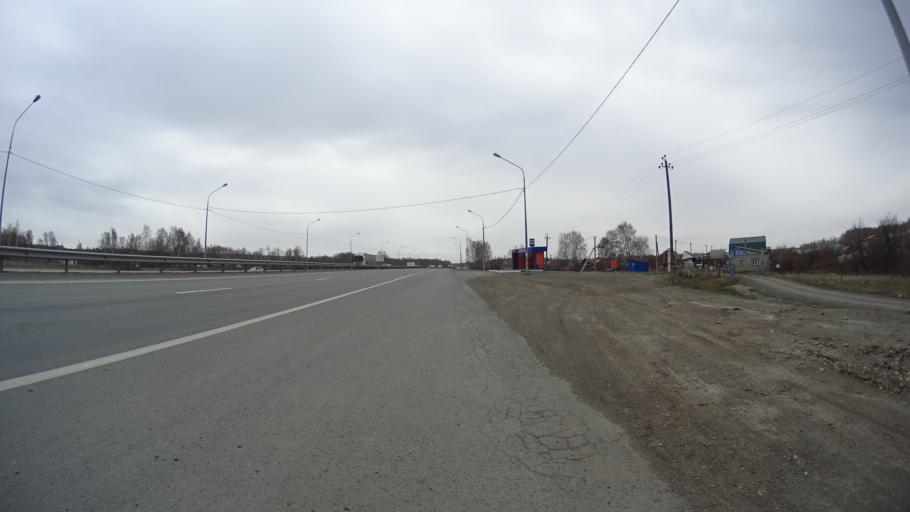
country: RU
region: Chelyabinsk
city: Novosineglazovskiy
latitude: 54.9799
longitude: 61.4165
